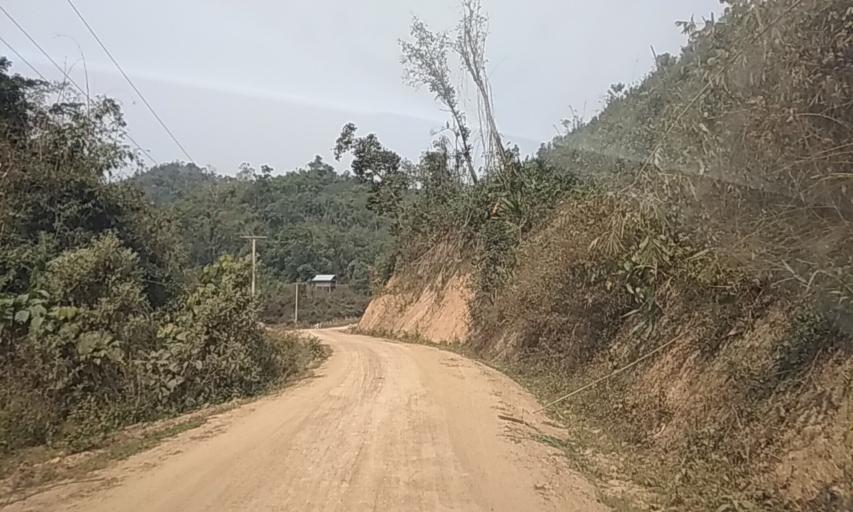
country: VN
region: Huyen Dien Bien
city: Dien Bien Phu
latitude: 21.4194
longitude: 102.7603
